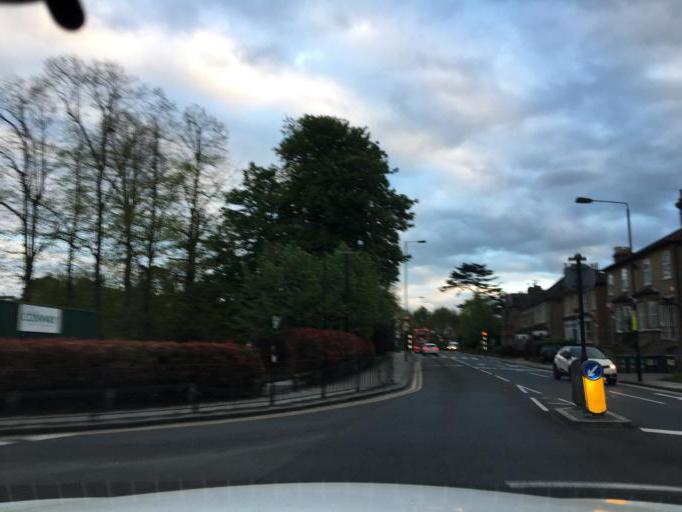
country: GB
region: England
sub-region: Greater London
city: Sidcup
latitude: 51.4250
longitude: 0.1010
